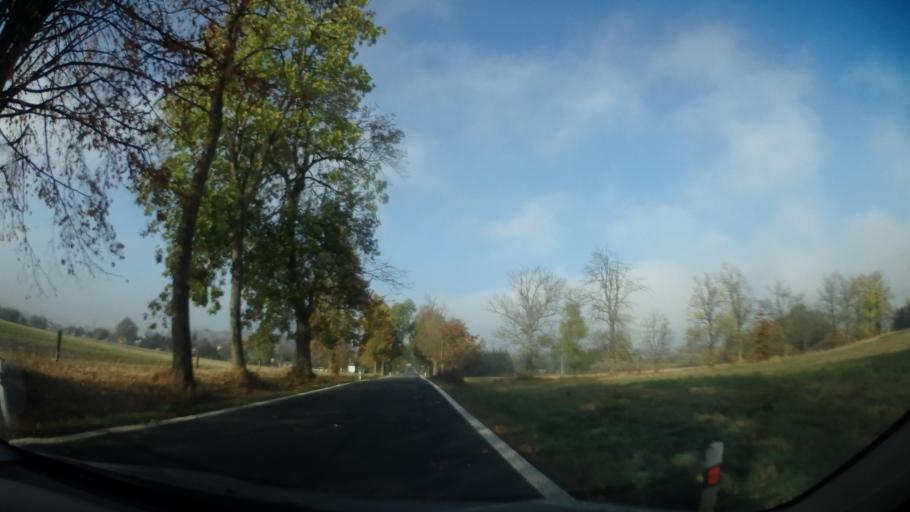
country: CZ
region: Vysocina
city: Krizanov
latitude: 49.4389
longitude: 16.1525
